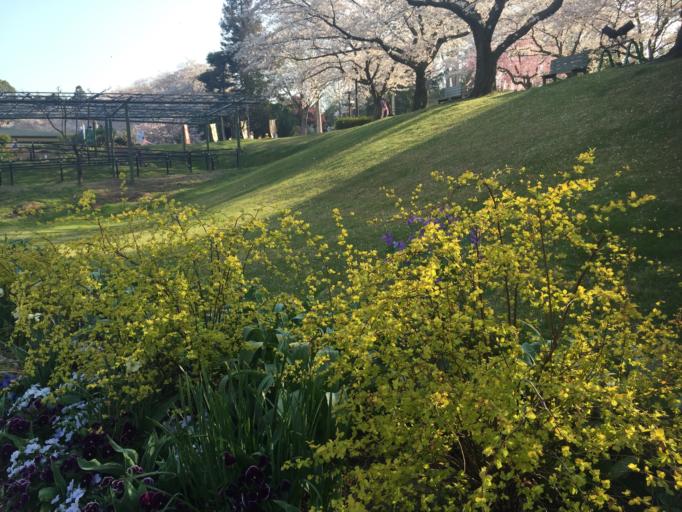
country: JP
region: Shizuoka
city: Kosai-shi
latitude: 34.7636
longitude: 137.6355
